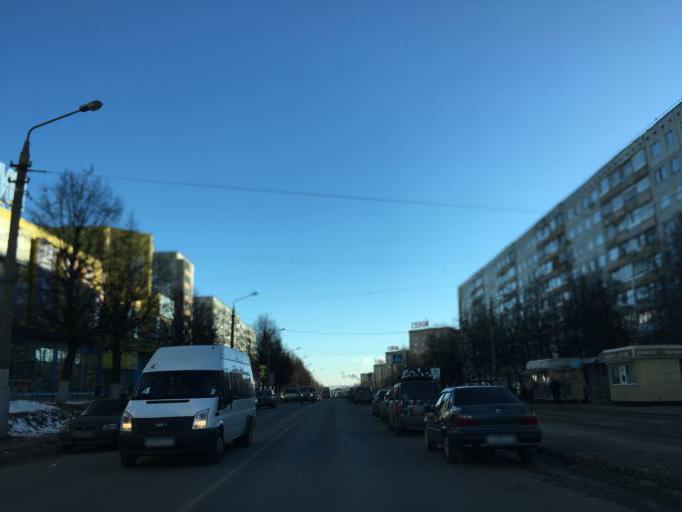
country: RU
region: Tula
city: Tula
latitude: 54.1920
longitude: 37.6875
